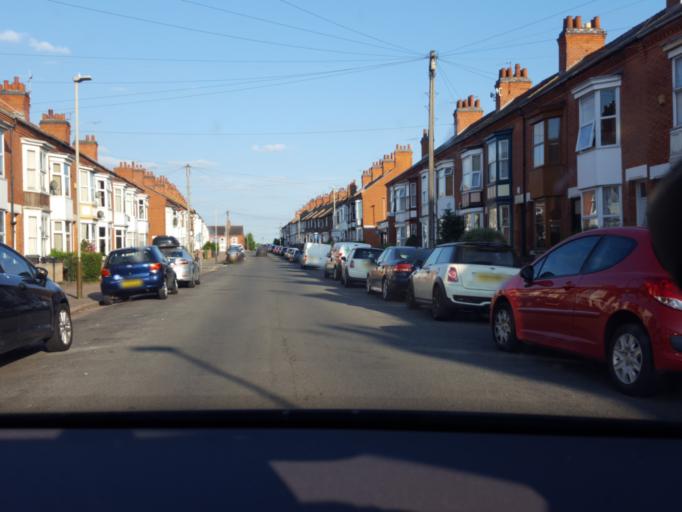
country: GB
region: England
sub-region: City of Leicester
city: Leicester
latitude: 52.6207
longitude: -1.1554
